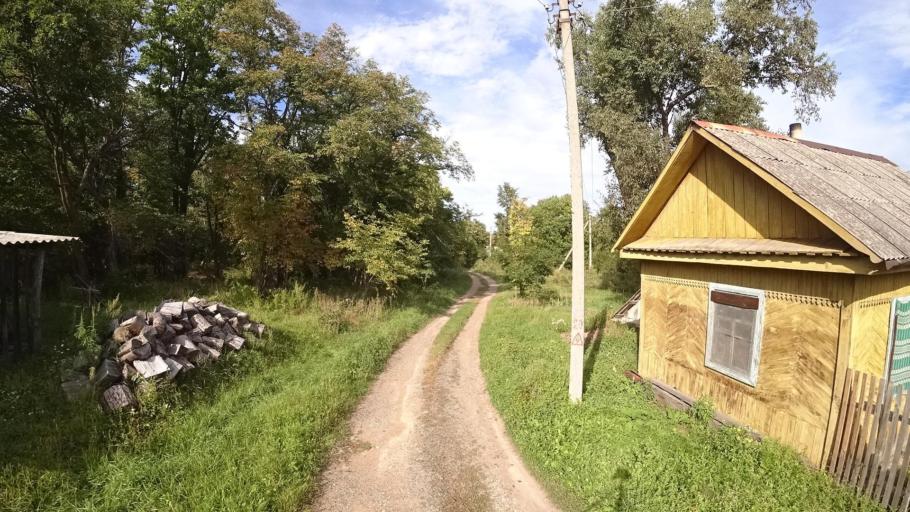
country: RU
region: Primorskiy
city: Dostoyevka
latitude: 44.2928
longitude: 133.4581
